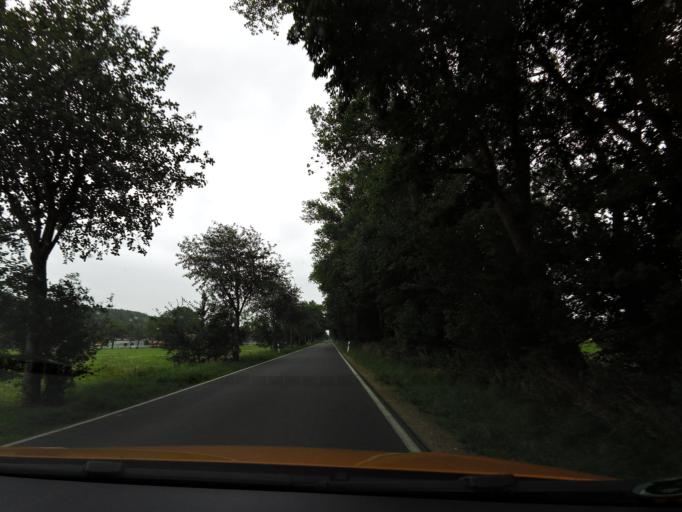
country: DE
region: Lower Saxony
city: Wirdum
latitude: 53.5137
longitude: 7.1402
